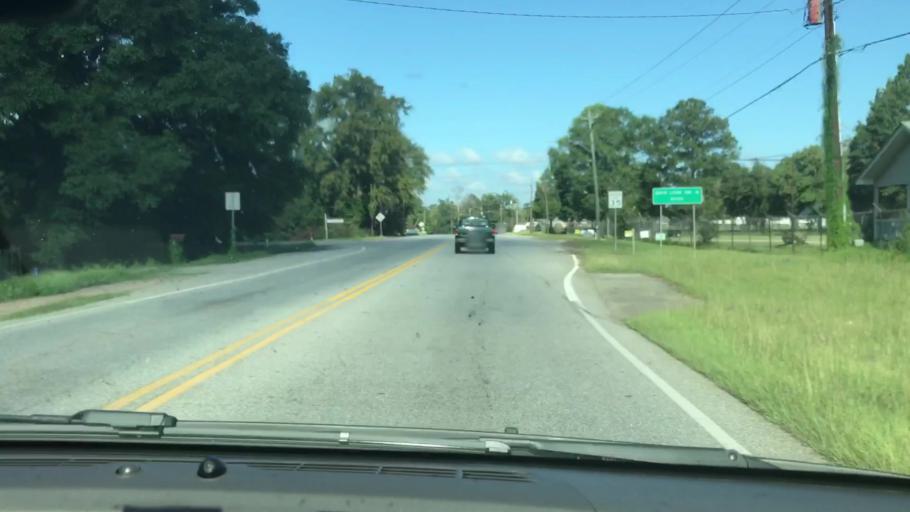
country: US
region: Georgia
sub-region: Quitman County
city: Georgetown
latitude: 31.8839
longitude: -85.0974
